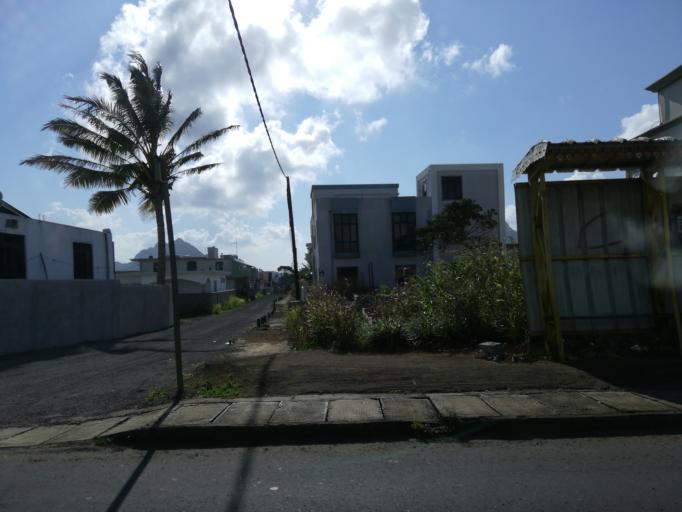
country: MU
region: Moka
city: Verdun
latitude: -20.2216
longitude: 57.5477
